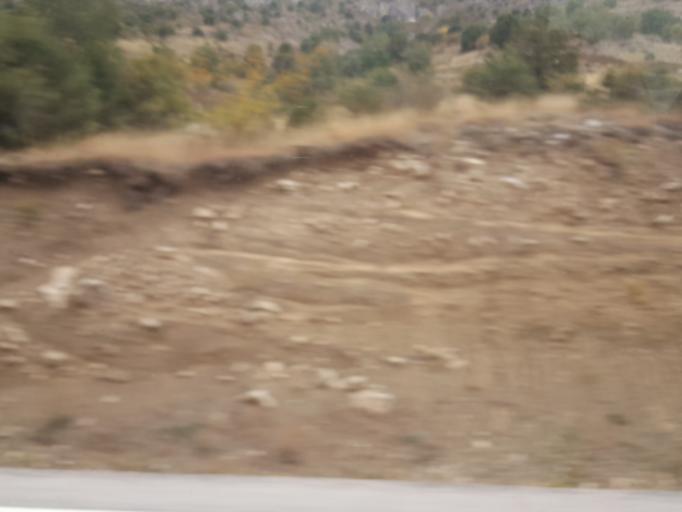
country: TR
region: Yozgat
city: Cekerek
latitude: 40.2088
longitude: 35.4856
